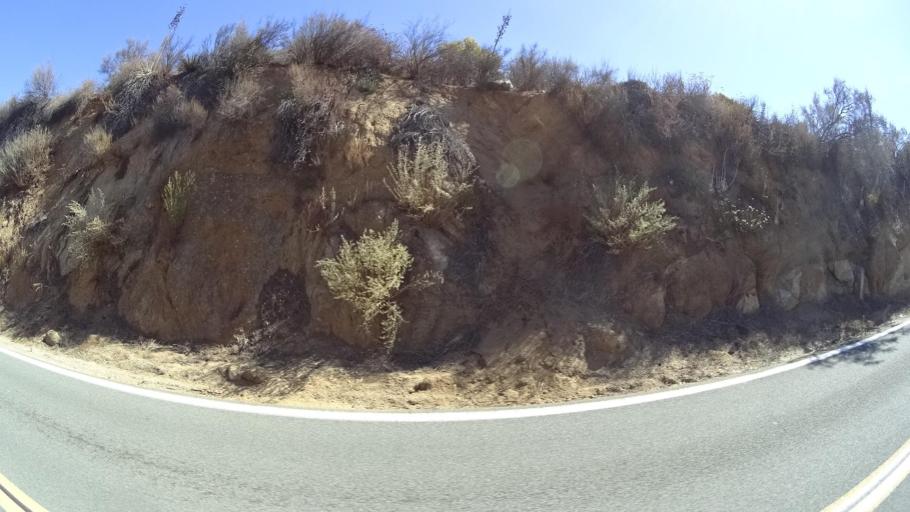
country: US
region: California
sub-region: San Diego County
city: Descanso
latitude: 32.7621
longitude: -116.6742
